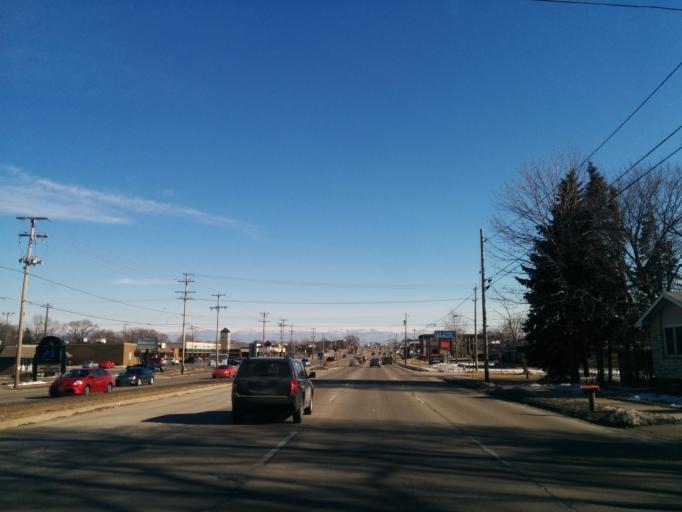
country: US
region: Wisconsin
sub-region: Racine County
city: Sturtevant
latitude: 42.7192
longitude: -87.8584
